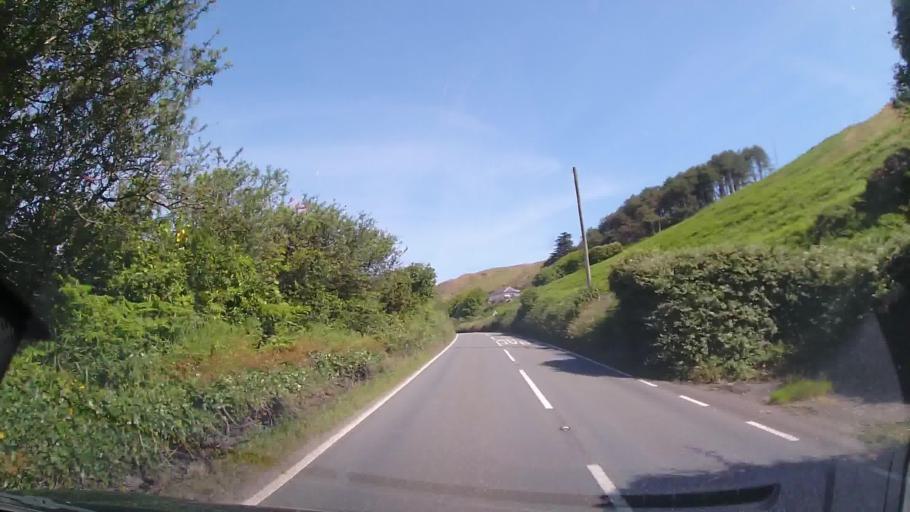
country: GB
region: Wales
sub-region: Gwynedd
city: Tywyn
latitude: 52.5503
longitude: -4.0701
